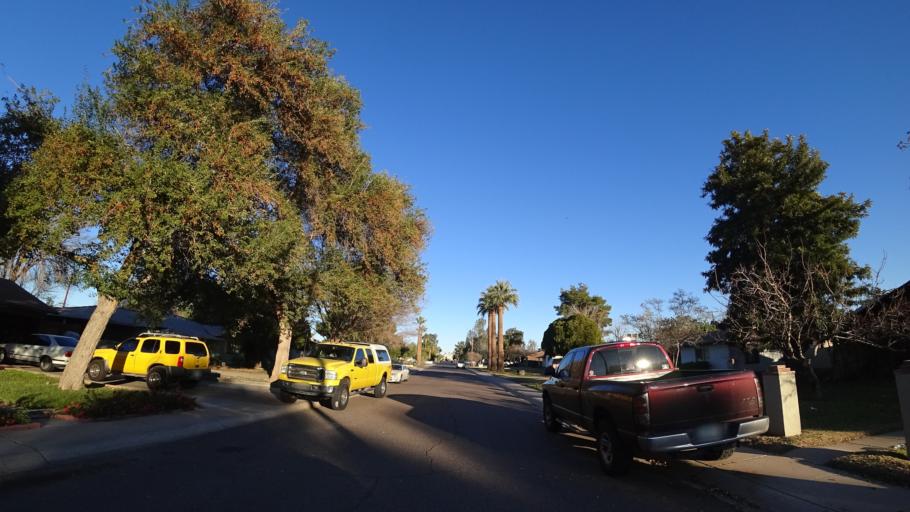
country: US
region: Arizona
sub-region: Maricopa County
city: Phoenix
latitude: 33.4866
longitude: -112.0345
